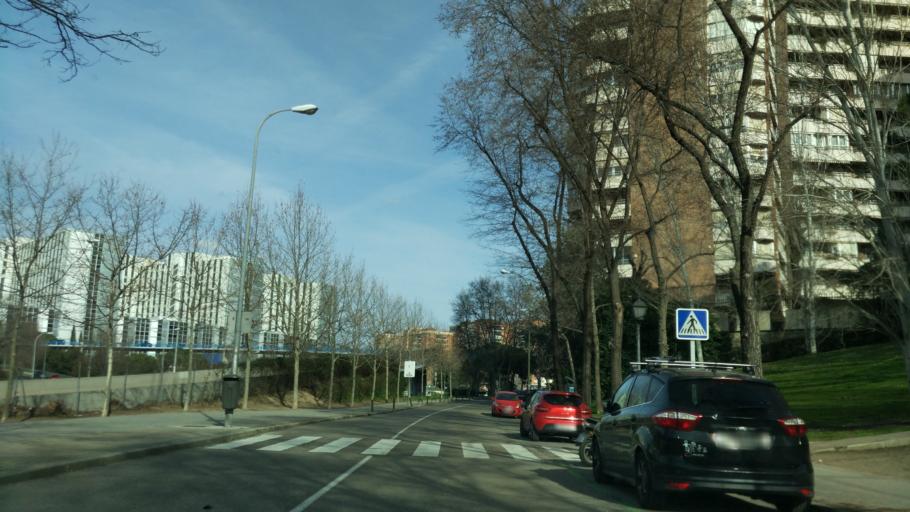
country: ES
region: Madrid
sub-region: Provincia de Madrid
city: Tetuan de las Victorias
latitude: 40.4843
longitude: -3.6975
